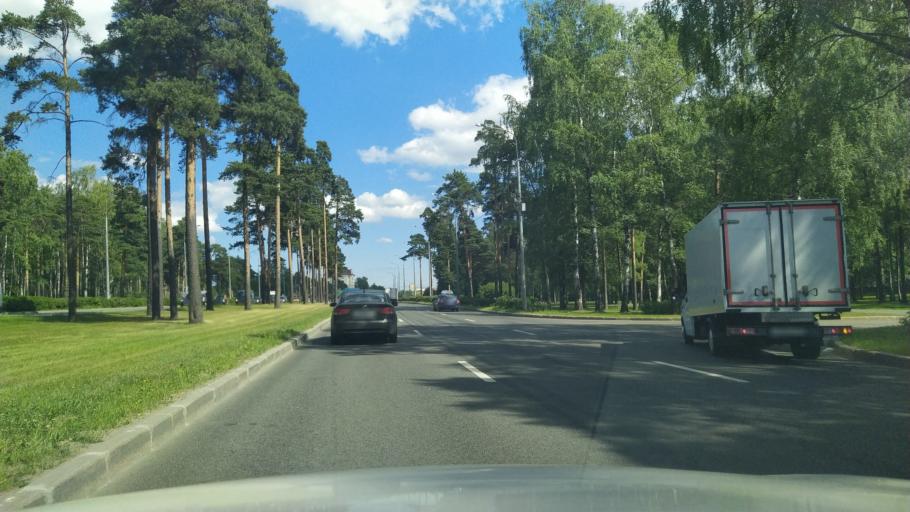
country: RU
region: Leningrad
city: Kalininskiy
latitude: 59.9947
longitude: 30.4011
